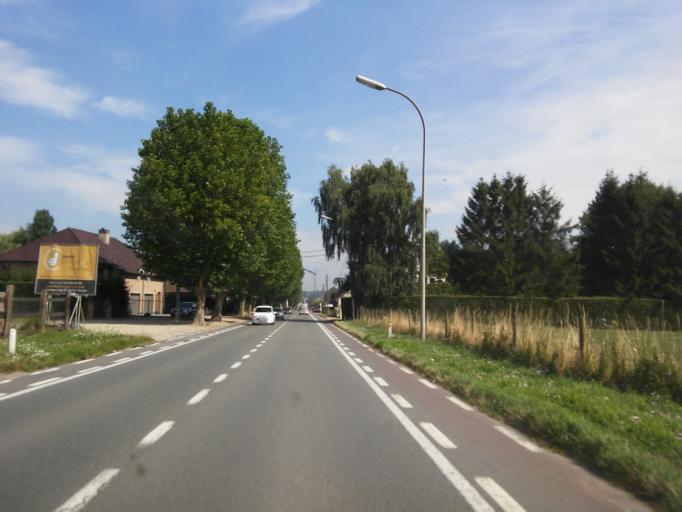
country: BE
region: Flanders
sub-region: Provincie Vlaams-Brabant
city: Ternat
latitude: 50.8648
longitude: 4.1585
